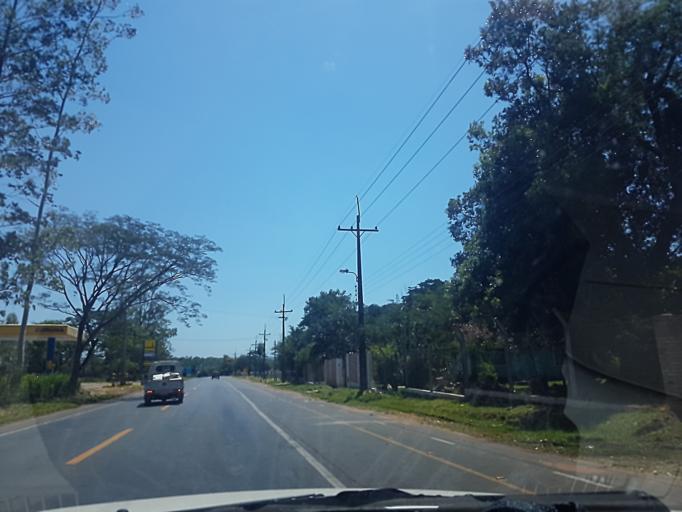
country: PY
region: Central
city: Aregua
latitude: -25.2389
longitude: -57.4250
